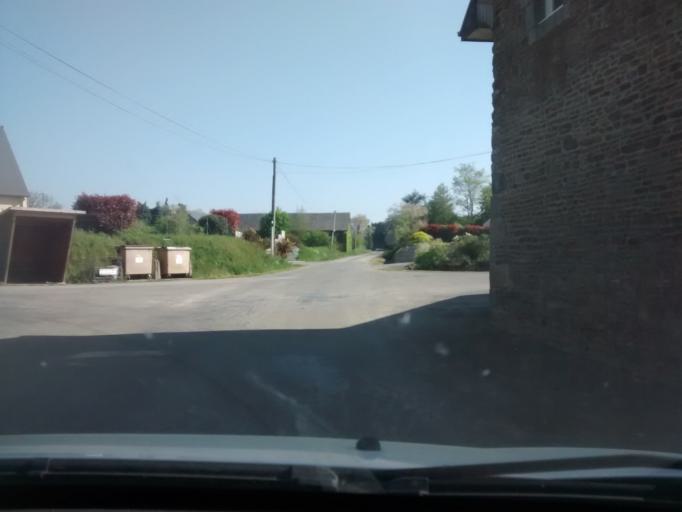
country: FR
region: Brittany
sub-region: Departement d'Ille-et-Vilaine
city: Javene
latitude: 48.3008
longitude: -1.2214
